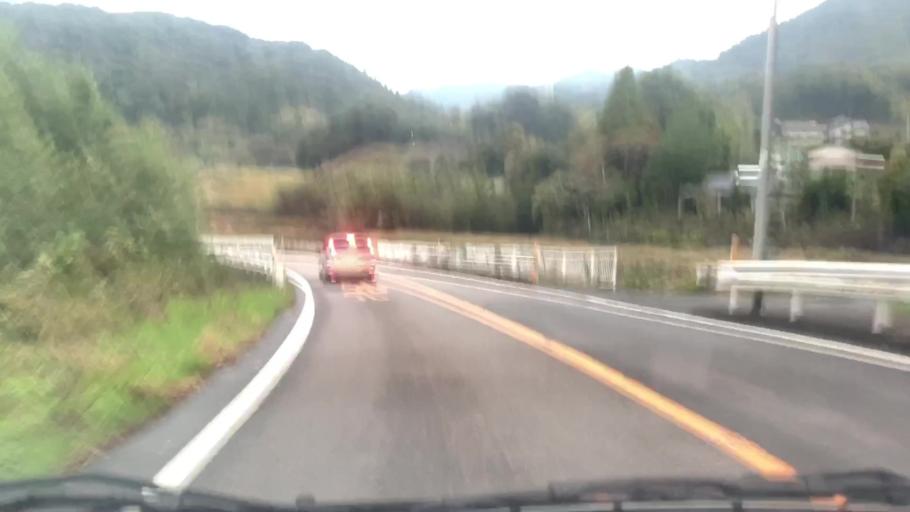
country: JP
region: Saga Prefecture
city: Ureshinomachi-shimojuku
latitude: 33.0545
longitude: 129.9374
